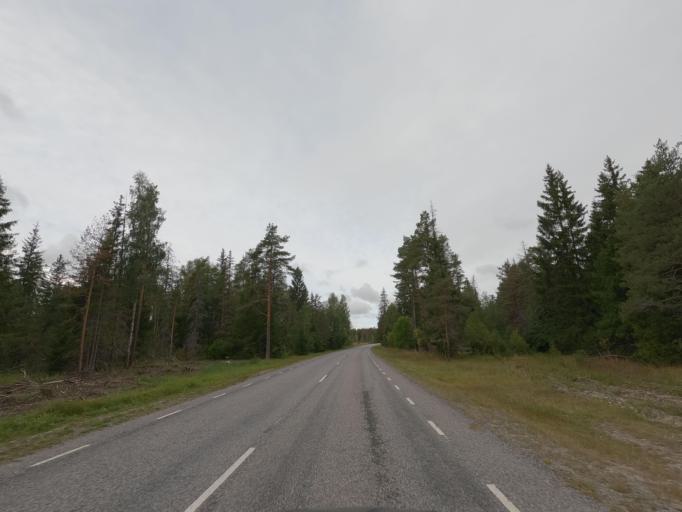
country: EE
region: Raplamaa
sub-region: Rapla vald
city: Rapla
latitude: 59.0056
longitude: 24.6223
